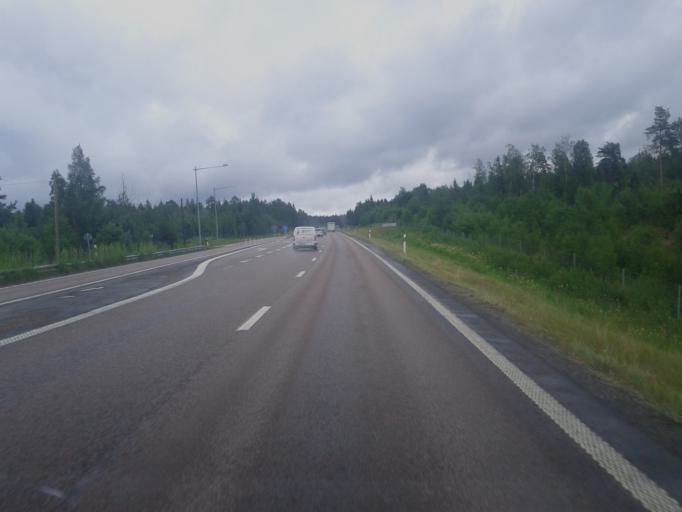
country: SE
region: Vaesternorrland
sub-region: Timra Kommun
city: Soraker
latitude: 62.5306
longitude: 17.4923
